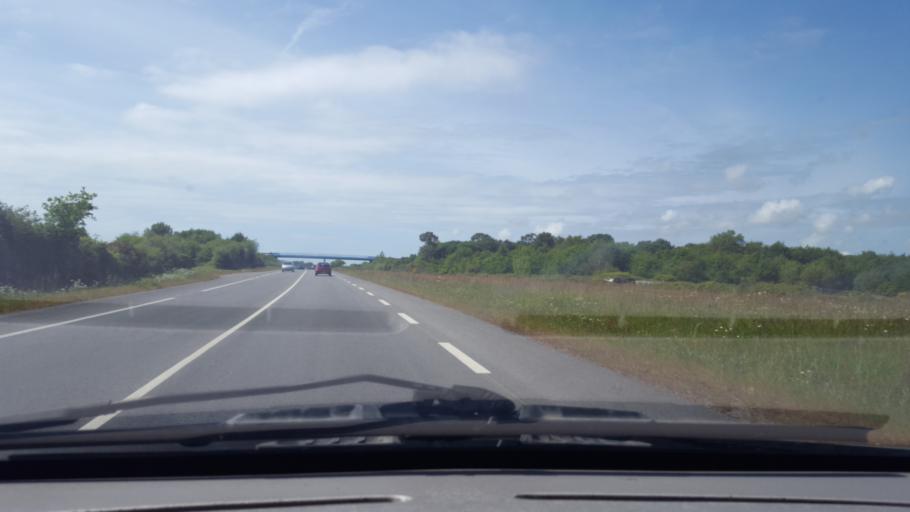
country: FR
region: Pays de la Loire
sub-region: Departement de la Loire-Atlantique
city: Les Moutiers-en-Retz
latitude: 47.0702
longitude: -1.9902
